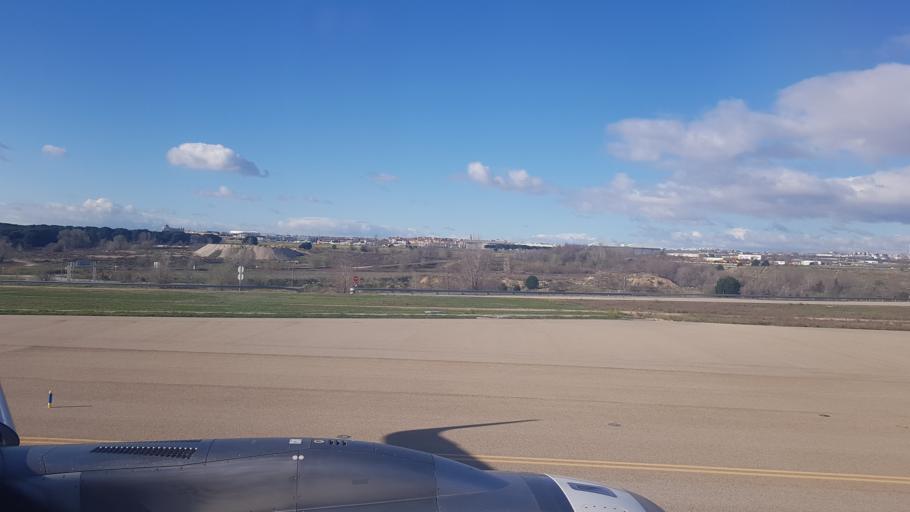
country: ES
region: Madrid
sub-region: Provincia de Madrid
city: Barajas de Madrid
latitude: 40.4889
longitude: -3.5547
